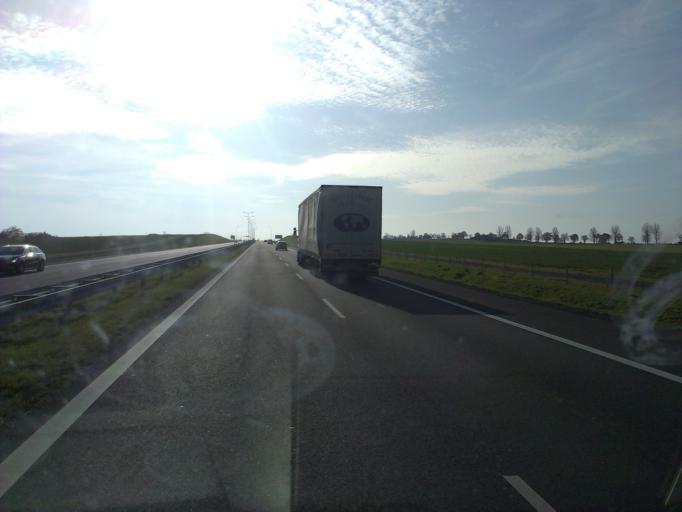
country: PL
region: Lubusz
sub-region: Powiat swiebodzinski
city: Swiebodzin
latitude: 52.2865
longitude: 15.5413
